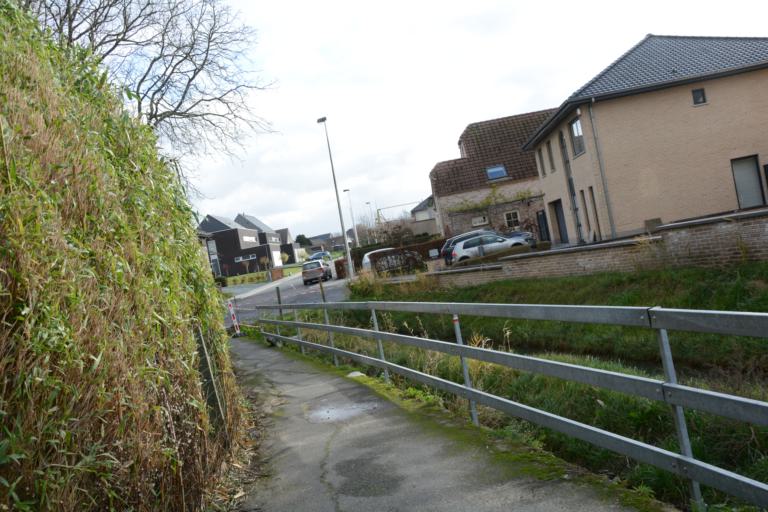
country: BE
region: Flanders
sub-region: Provincie Vlaams-Brabant
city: Opwijk
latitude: 50.9419
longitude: 4.1729
